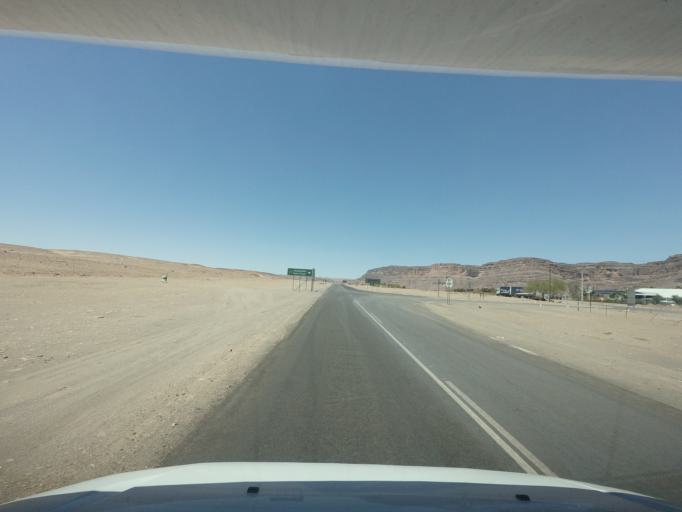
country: ZA
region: Northern Cape
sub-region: Namakwa District Municipality
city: Port Nolloth
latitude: -28.7357
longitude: 17.6171
